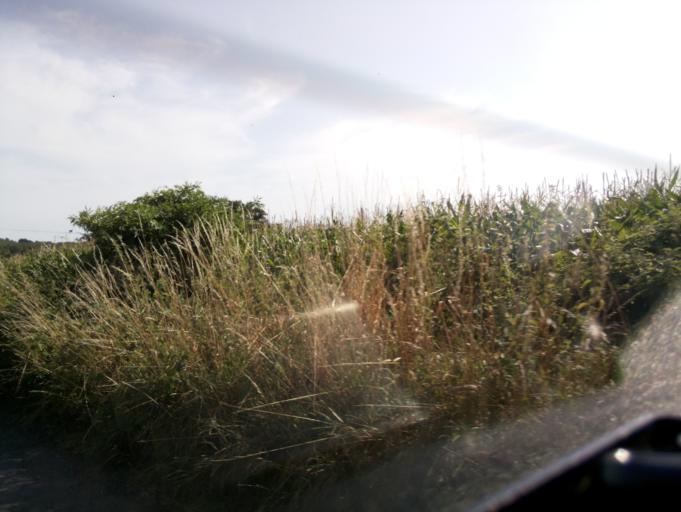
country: GB
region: England
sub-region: Gloucestershire
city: Dursley
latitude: 51.7002
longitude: -2.3447
